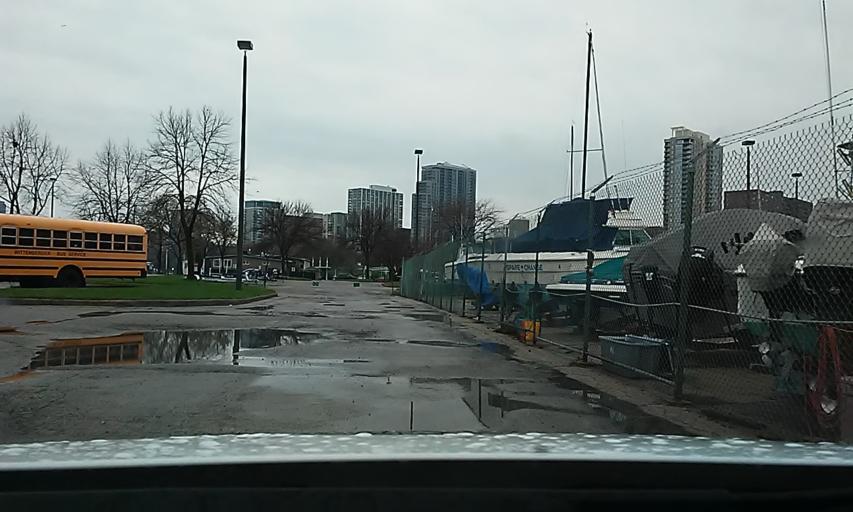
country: US
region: Wisconsin
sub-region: Milwaukee County
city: Milwaukee
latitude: 43.0525
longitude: -87.8834
